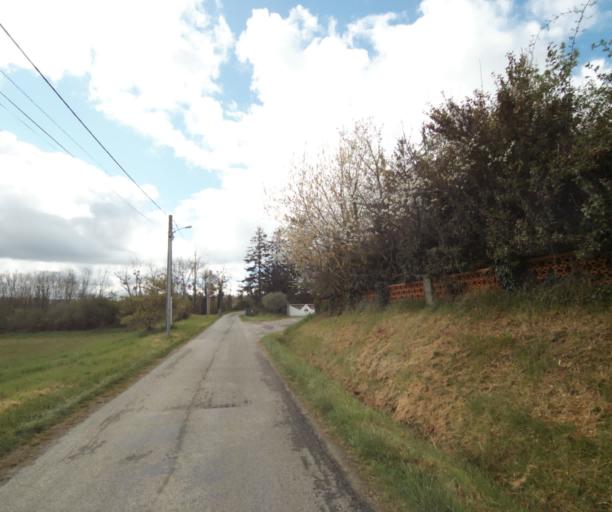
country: FR
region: Midi-Pyrenees
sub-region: Departement de l'Ariege
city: Saverdun
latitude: 43.2102
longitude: 1.5758
